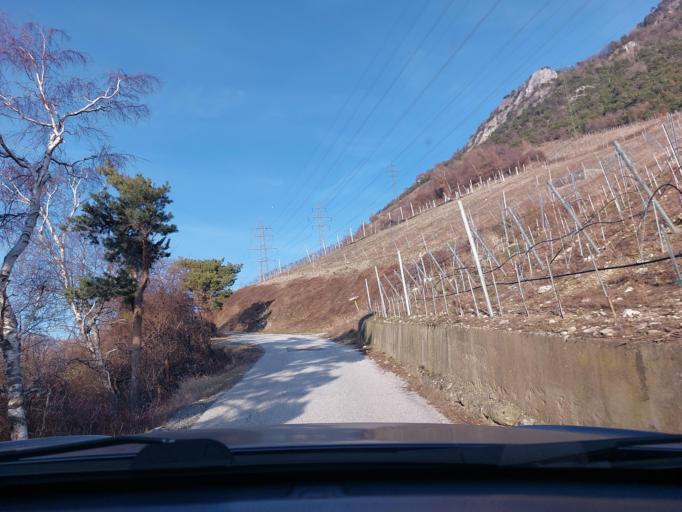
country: CH
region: Valais
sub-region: Martigny District
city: Charrat-les-Chenes
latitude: 46.1343
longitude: 7.1569
